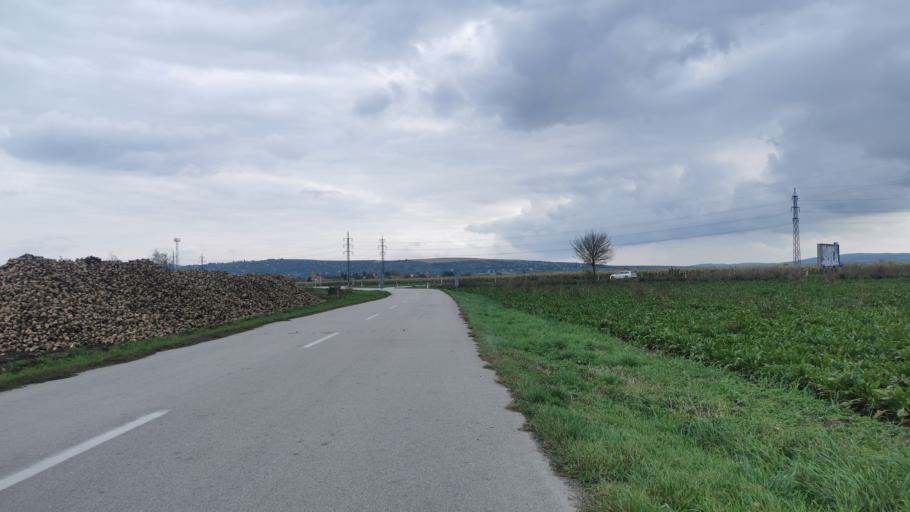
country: SK
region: Trnavsky
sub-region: Okres Skalica
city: Holic
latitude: 48.8275
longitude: 17.1791
